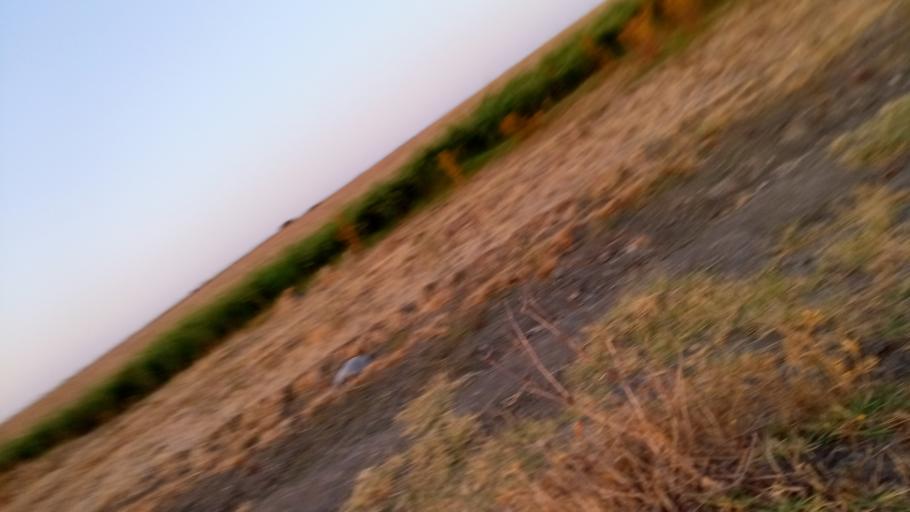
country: PT
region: Evora
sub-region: Reguengos de Monsaraz
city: Reguengos de Monsaraz
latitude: 38.3614
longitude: -7.4600
